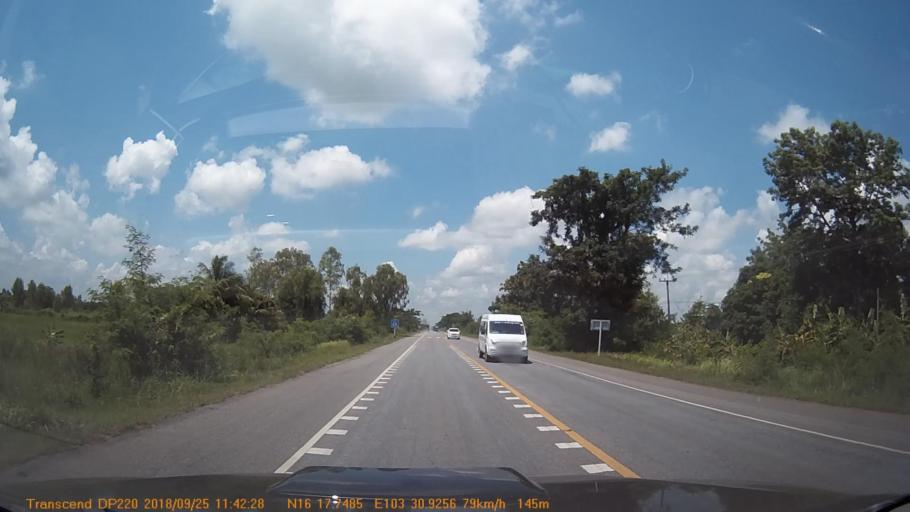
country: TH
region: Kalasin
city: Khong Chai
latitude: 16.2958
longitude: 103.5155
